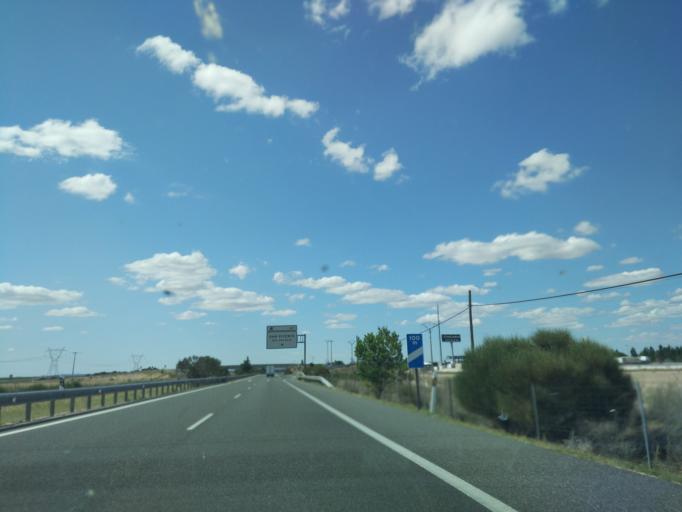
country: ES
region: Castille and Leon
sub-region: Provincia de Valladolid
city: San Vicente del Palacio
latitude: 41.2184
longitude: -4.8404
